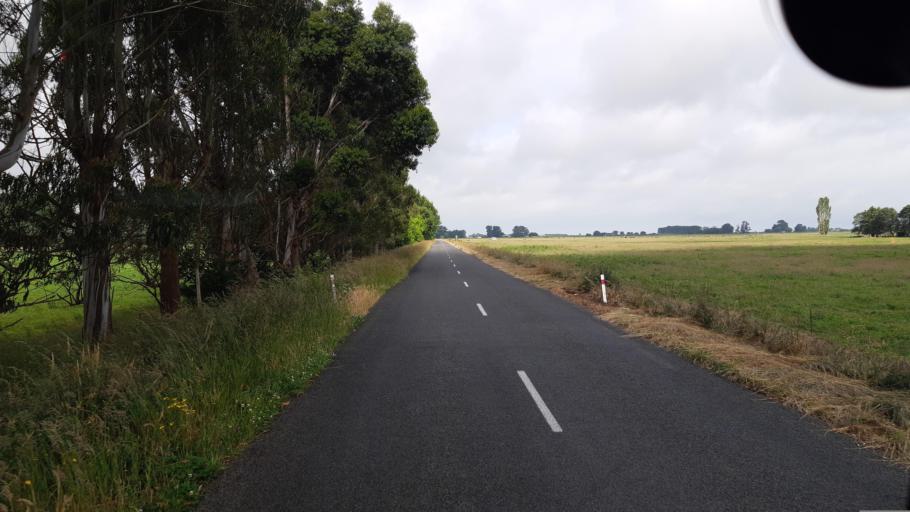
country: NZ
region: Canterbury
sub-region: Timaru District
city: Timaru
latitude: -44.2450
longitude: 171.3190
